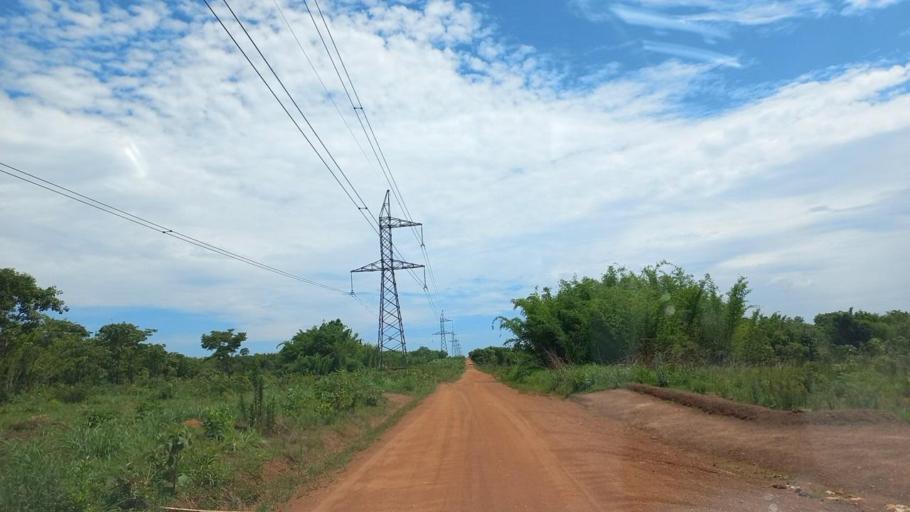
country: ZM
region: Copperbelt
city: Kitwe
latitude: -12.8109
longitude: 28.3595
